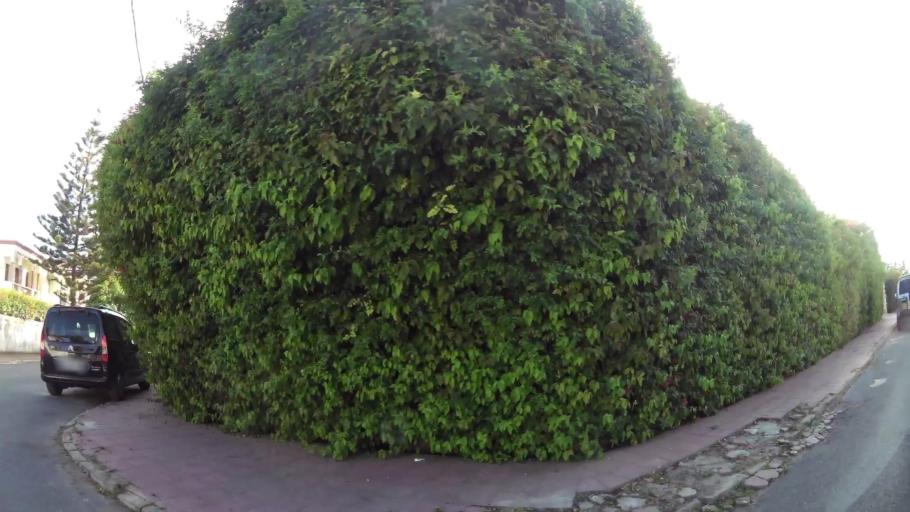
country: MA
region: Rabat-Sale-Zemmour-Zaer
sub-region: Rabat
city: Rabat
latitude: 33.9602
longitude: -6.8524
